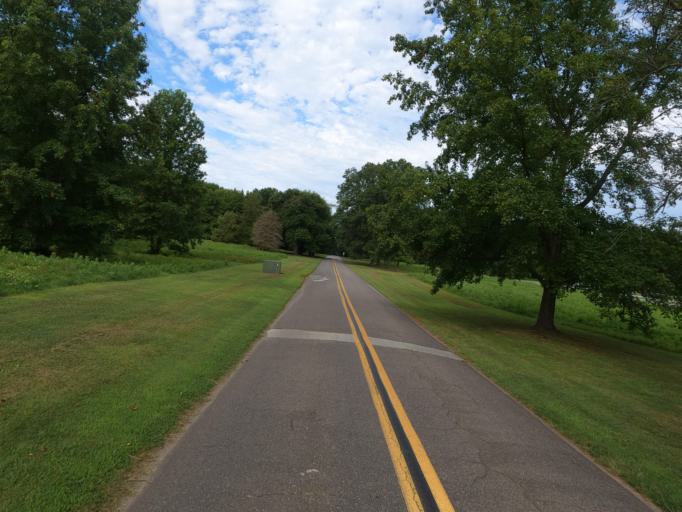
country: US
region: Delaware
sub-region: New Castle County
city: Glasgow
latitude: 39.5635
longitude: -75.7191
